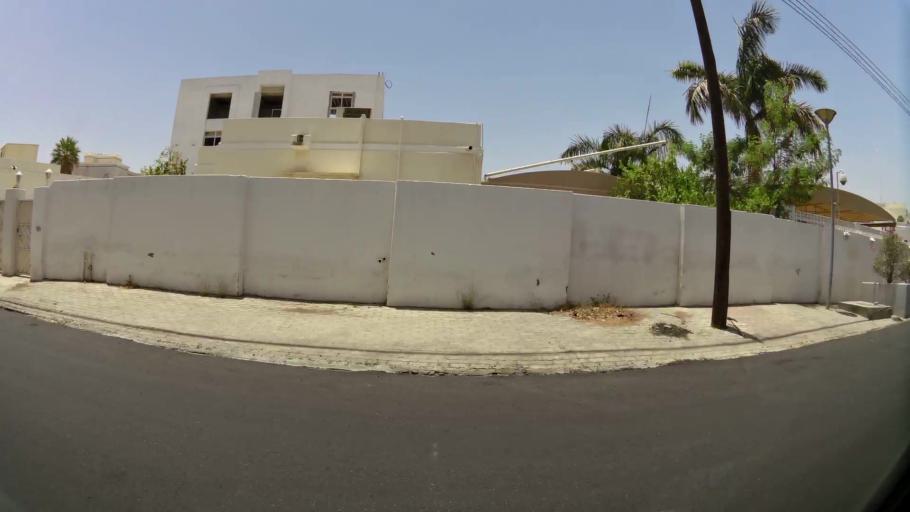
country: OM
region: Muhafazat Masqat
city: Bawshar
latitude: 23.6055
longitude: 58.4563
